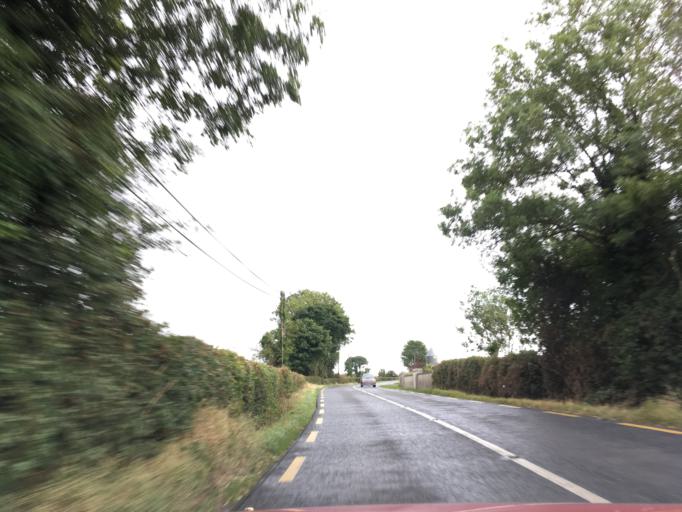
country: IE
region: Munster
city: Fethard
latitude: 52.4276
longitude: -7.7768
